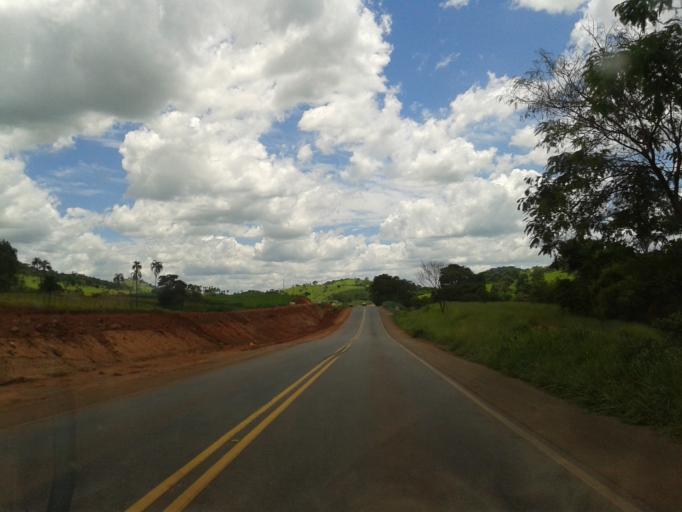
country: BR
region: Goias
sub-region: Petrolina De Goias
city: Petrolina de Goias
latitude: -16.2020
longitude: -49.3135
